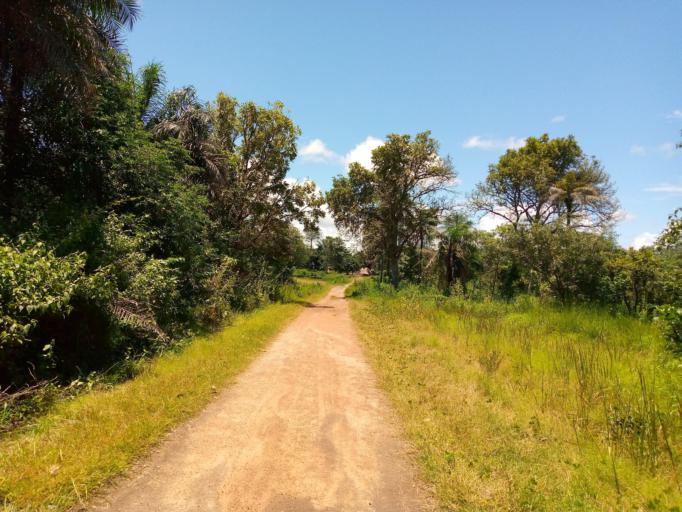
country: SL
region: Northern Province
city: Binkolo
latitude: 9.1024
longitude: -12.1412
